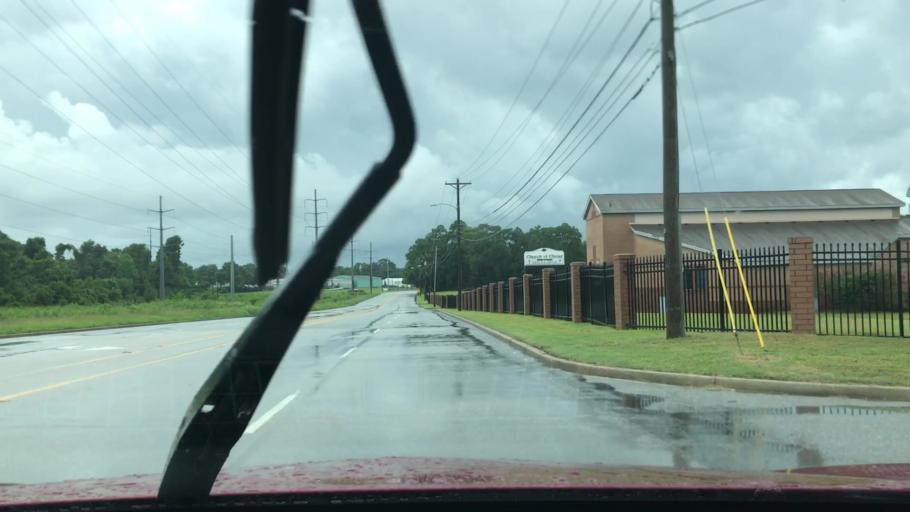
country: US
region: South Carolina
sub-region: Charleston County
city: North Charleston
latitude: 32.8471
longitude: -79.9963
